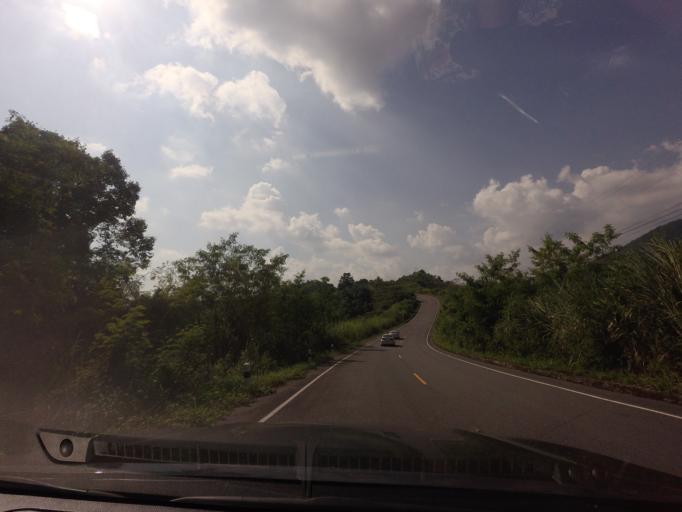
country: TH
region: Nan
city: Santi Suk
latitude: 18.9770
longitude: 101.0080
